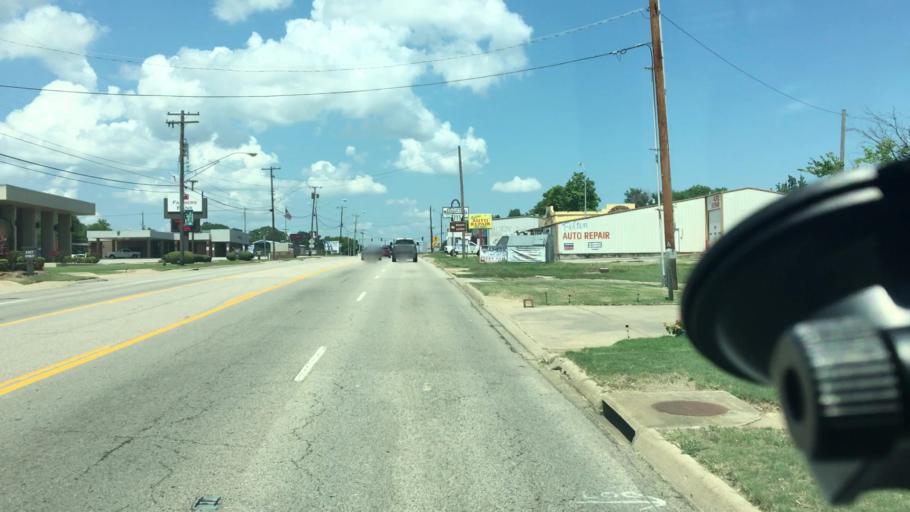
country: US
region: Arkansas
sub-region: Sebastian County
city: Barling
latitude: 35.3241
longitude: -94.2988
